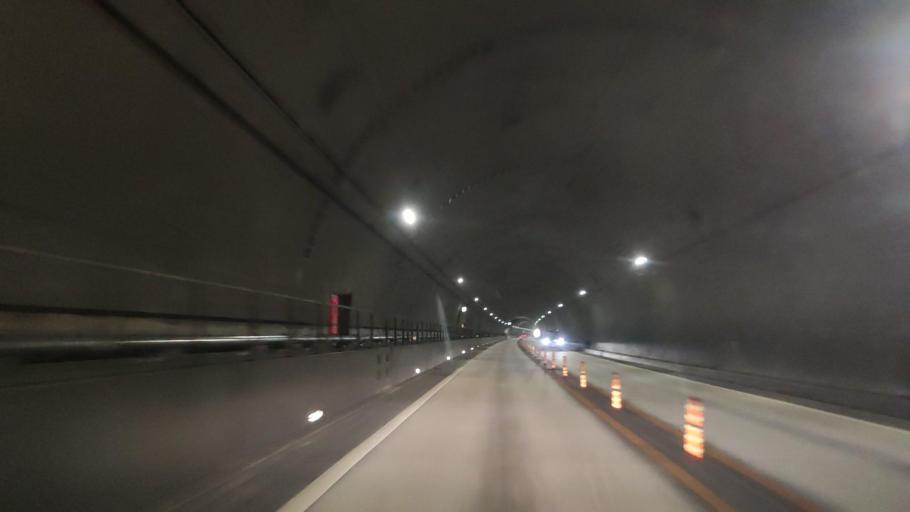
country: JP
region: Ehime
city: Hojo
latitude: 34.0812
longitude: 132.9768
